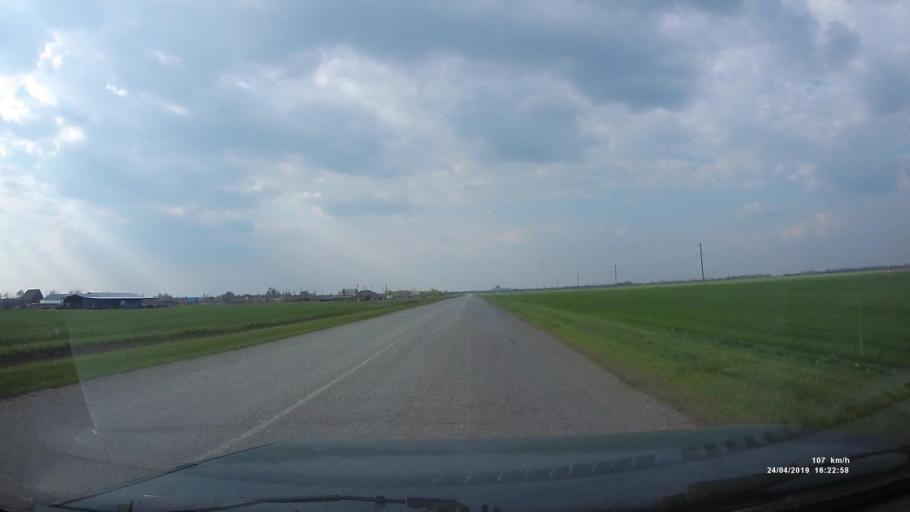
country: RU
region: Rostov
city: Orlovskiy
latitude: 46.8274
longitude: 42.0524
